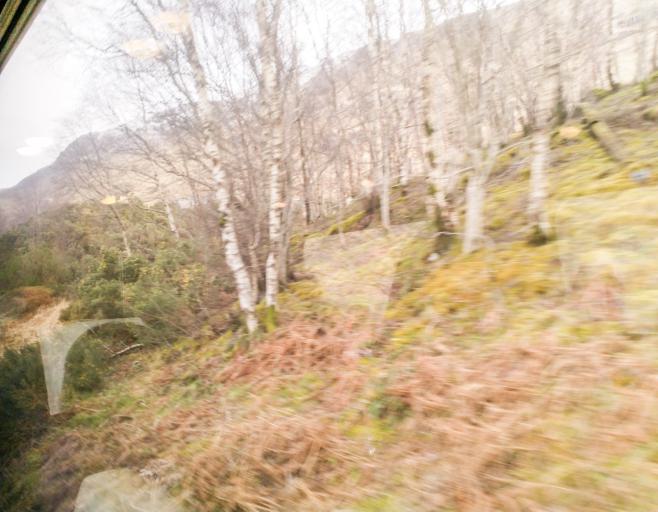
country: GB
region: Scotland
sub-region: Highland
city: Spean Bridge
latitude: 56.8198
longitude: -4.7137
